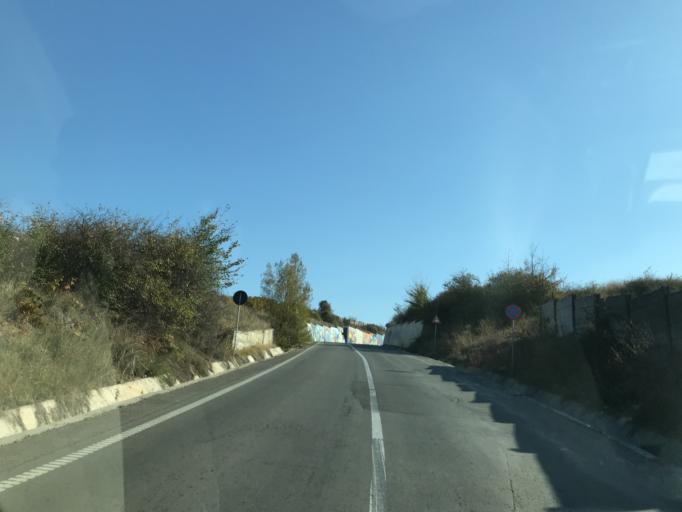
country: RO
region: Olt
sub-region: Municipiul Slatina
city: Slatina
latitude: 44.4414
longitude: 24.3513
